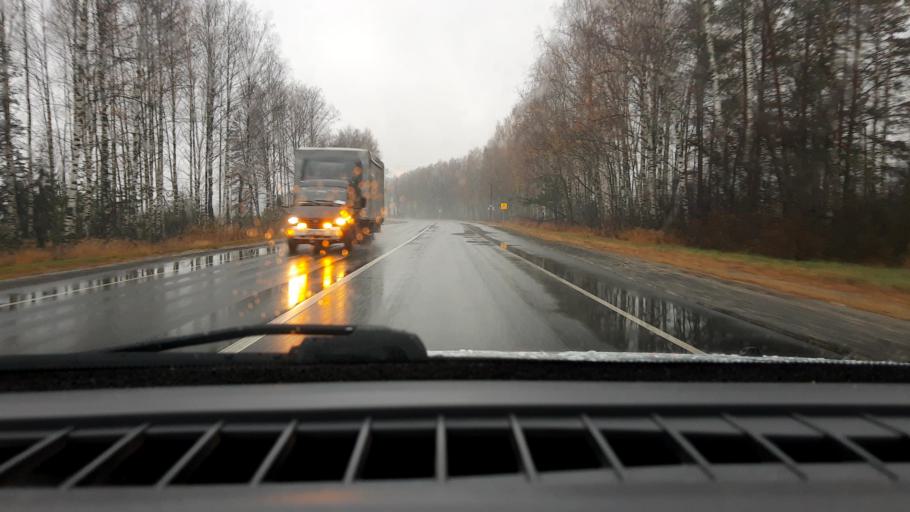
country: RU
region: Nizjnij Novgorod
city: Linda
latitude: 56.6592
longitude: 44.1260
